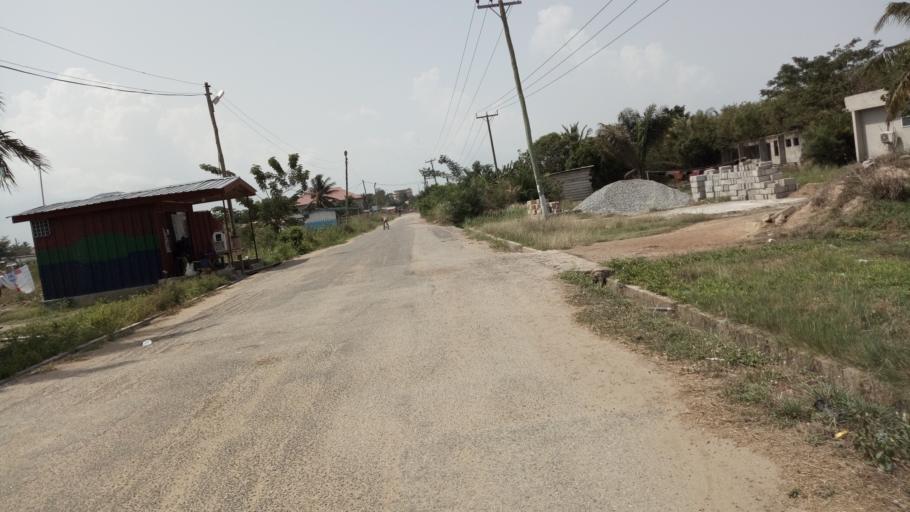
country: GH
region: Central
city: Winneba
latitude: 5.3609
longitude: -0.6359
